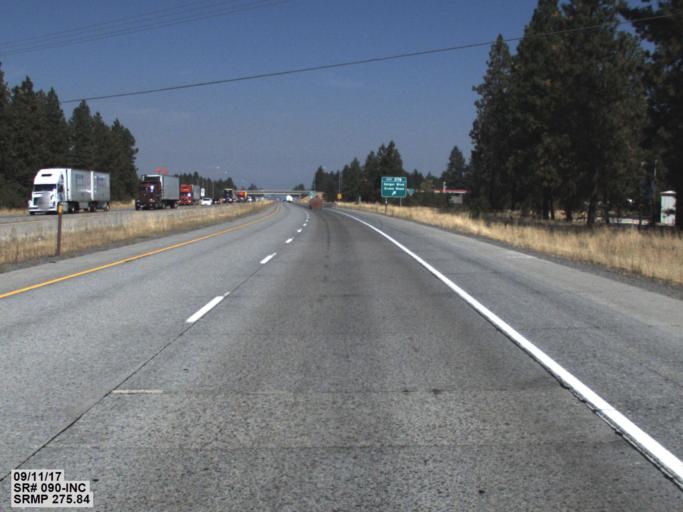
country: US
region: Washington
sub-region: Spokane County
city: Airway Heights
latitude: 47.6154
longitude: -117.5104
